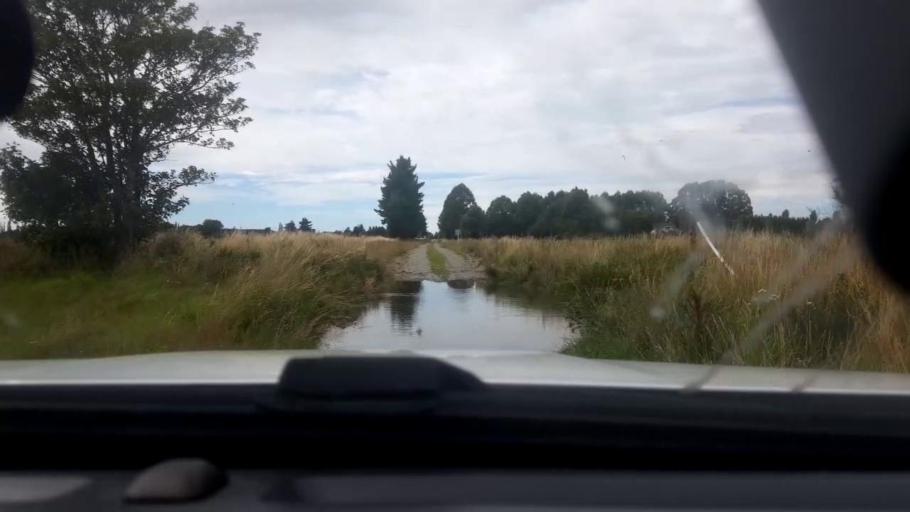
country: NZ
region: Canterbury
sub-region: Timaru District
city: Pleasant Point
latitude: -44.1334
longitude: 171.2850
